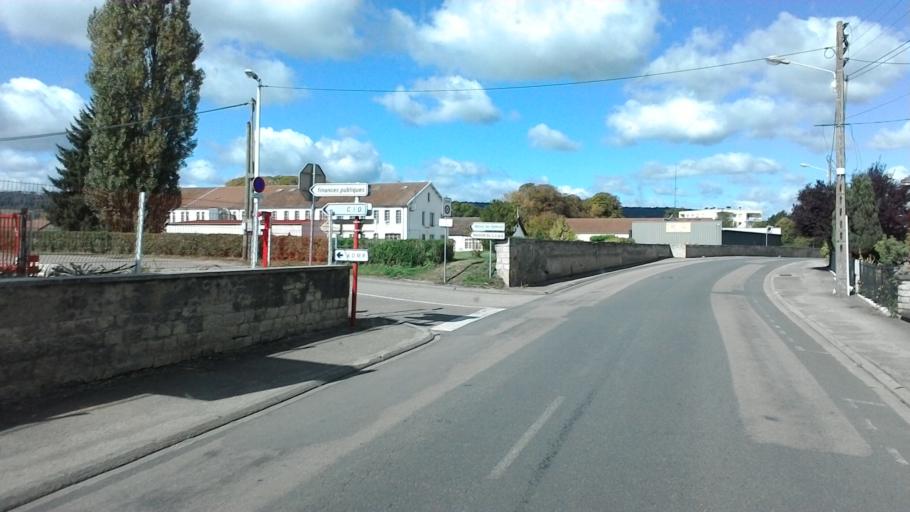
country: FR
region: Lorraine
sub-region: Departement des Vosges
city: Neufchateau
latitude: 48.3555
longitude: 5.6830
